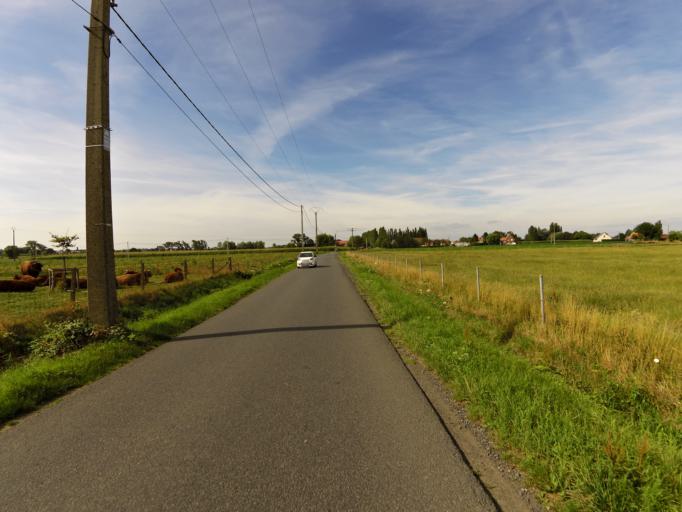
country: BE
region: Flanders
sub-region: Provincie West-Vlaanderen
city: Koekelare
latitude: 51.0562
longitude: 2.9969
